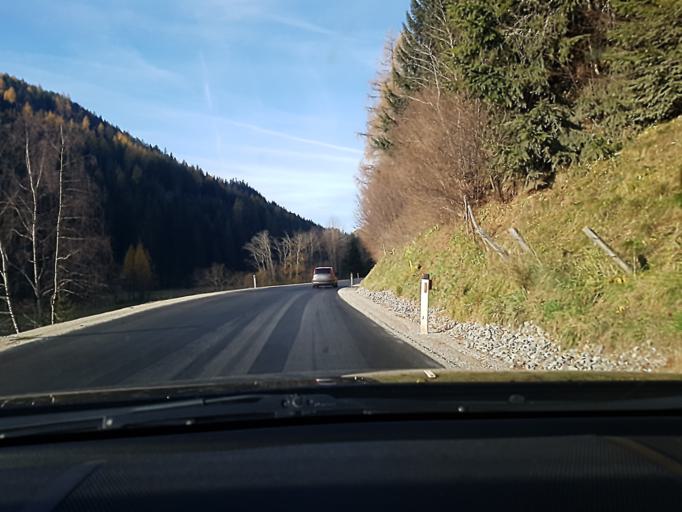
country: AT
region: Styria
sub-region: Politischer Bezirk Murau
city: Krakaudorf
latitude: 47.1648
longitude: 13.9972
